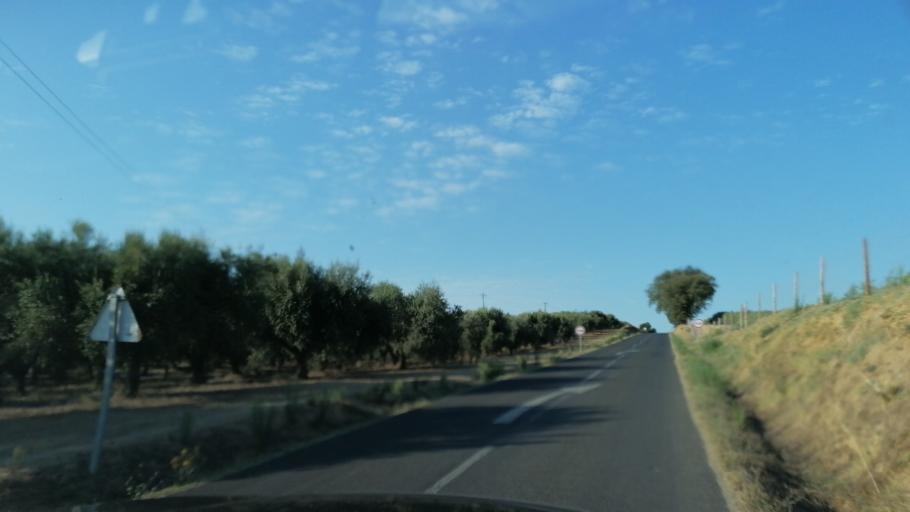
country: PT
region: Santarem
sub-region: Santarem
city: Santarem
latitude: 39.2742
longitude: -8.6617
